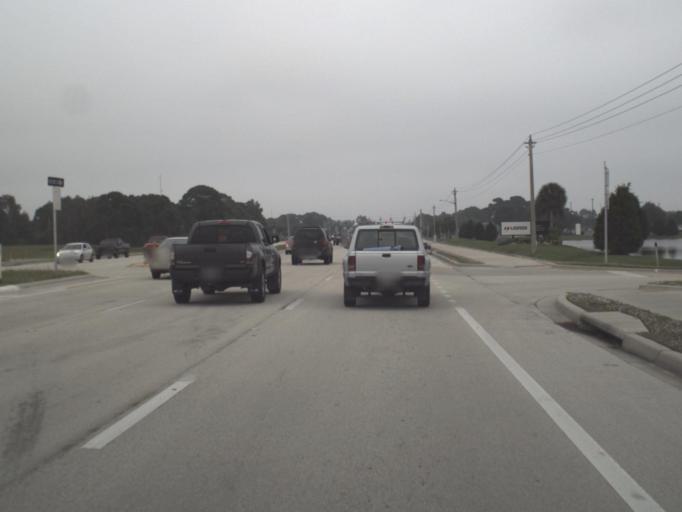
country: US
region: Florida
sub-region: Brevard County
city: Palm Bay
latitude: 28.0346
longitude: -80.6019
